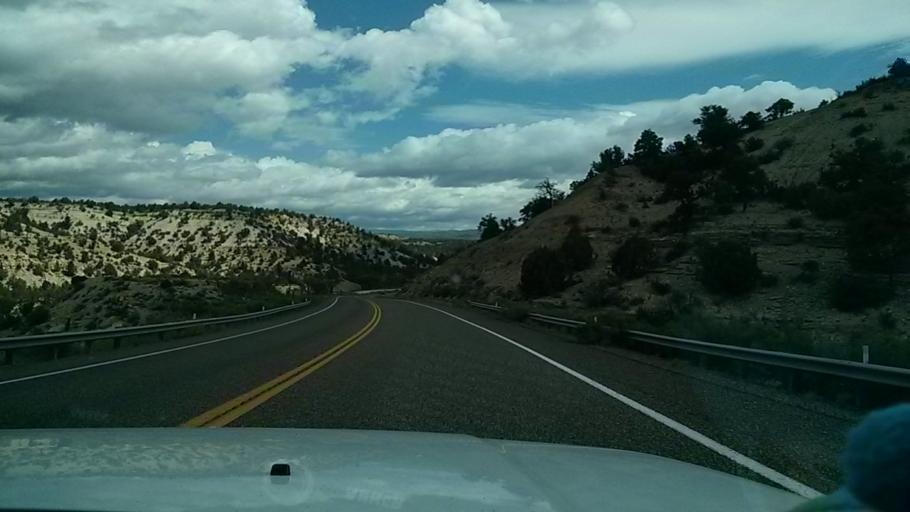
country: US
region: Utah
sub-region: Kane County
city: Kanab
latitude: 37.2107
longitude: -112.6841
